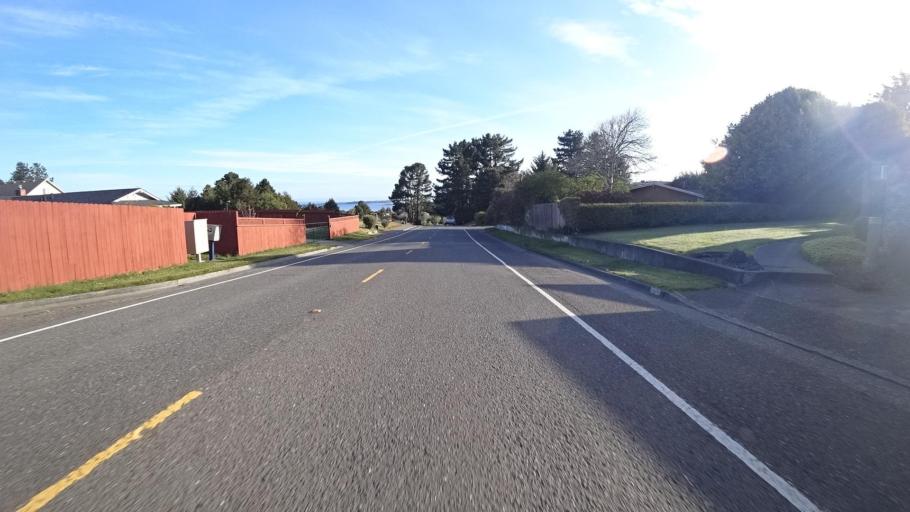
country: US
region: California
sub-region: Humboldt County
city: Humboldt Hill
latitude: 40.7194
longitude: -124.2032
